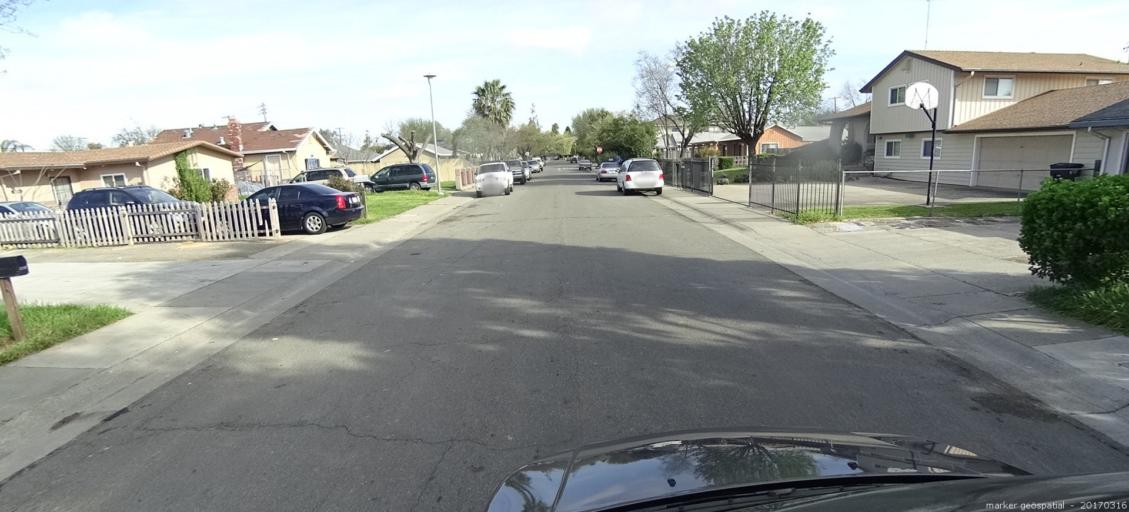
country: US
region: California
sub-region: Sacramento County
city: Parkway
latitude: 38.5127
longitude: -121.4804
